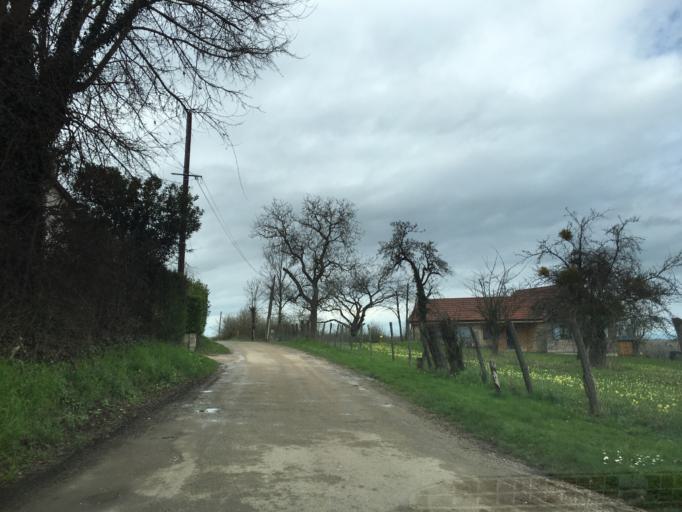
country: FR
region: Bourgogne
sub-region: Departement de l'Yonne
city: Fleury-la-Vallee
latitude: 47.8450
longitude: 3.4412
